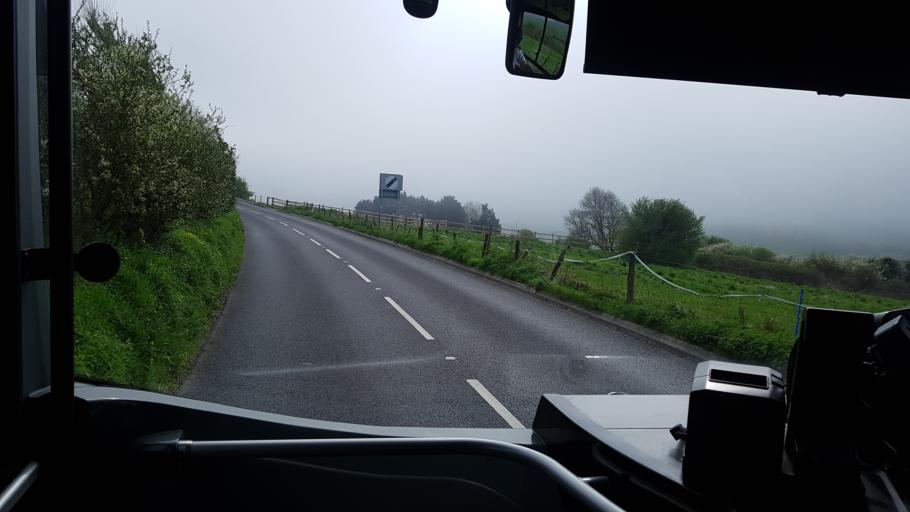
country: GB
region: England
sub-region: Isle of Wight
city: Ventnor
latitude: 50.6106
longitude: -1.2251
